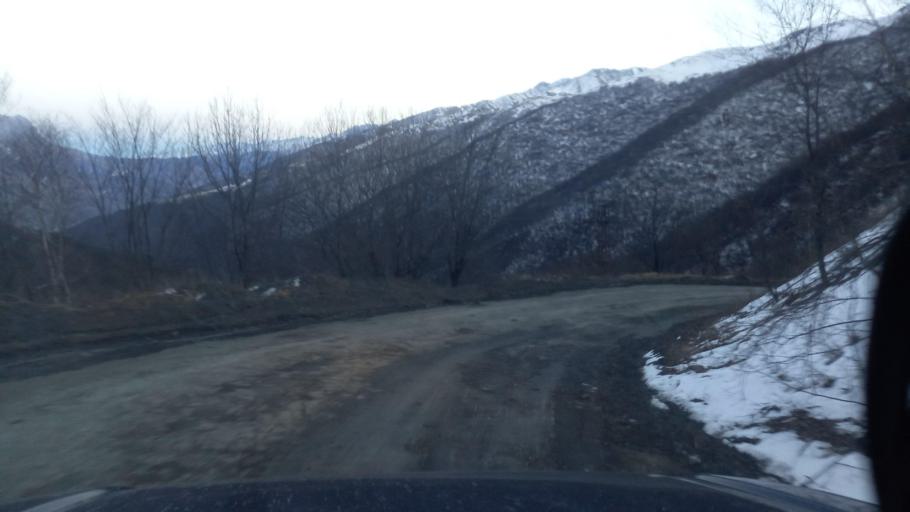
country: RU
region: Ingushetiya
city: Dzhayrakh
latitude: 42.8291
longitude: 44.5827
